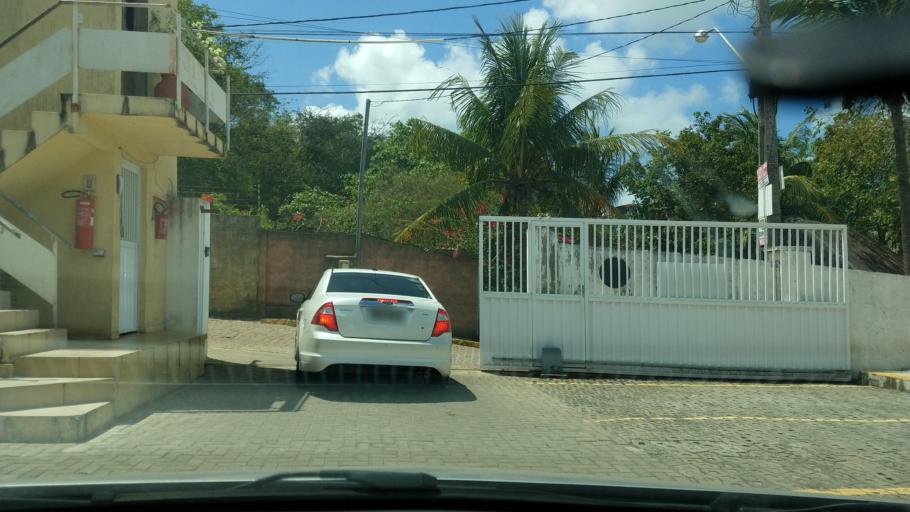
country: BR
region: Rio Grande do Norte
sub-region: Ares
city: Ares
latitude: -6.2316
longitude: -35.0524
